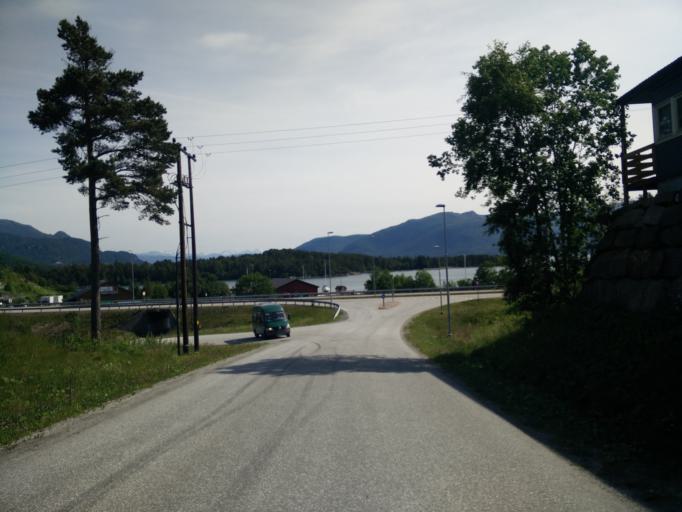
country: NO
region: More og Romsdal
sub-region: Kristiansund
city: Rensvik
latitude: 63.0118
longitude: 7.9699
